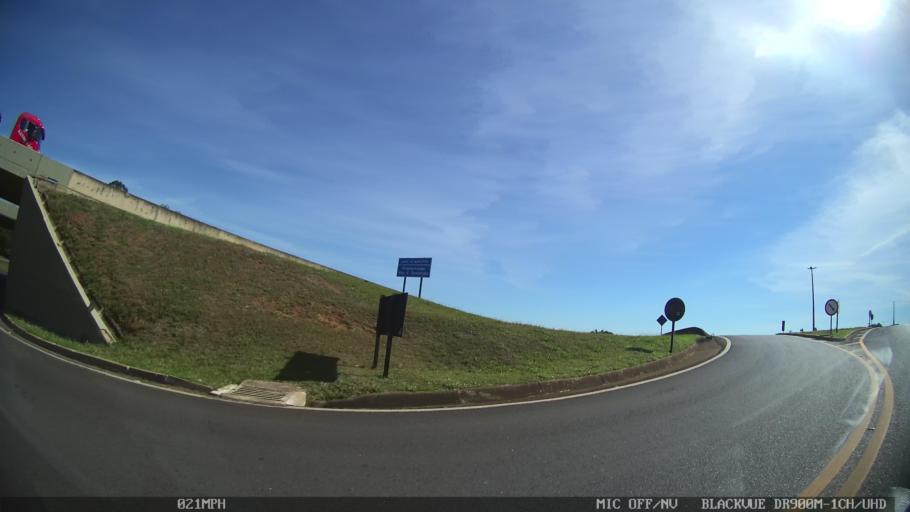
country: BR
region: Sao Paulo
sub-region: Pirassununga
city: Pirassununga
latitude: -22.0737
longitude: -47.4230
